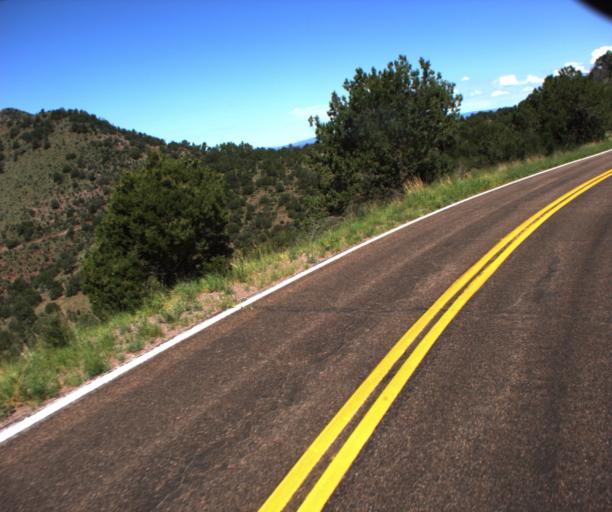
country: US
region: Arizona
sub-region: Greenlee County
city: Morenci
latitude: 33.2252
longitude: -109.3921
